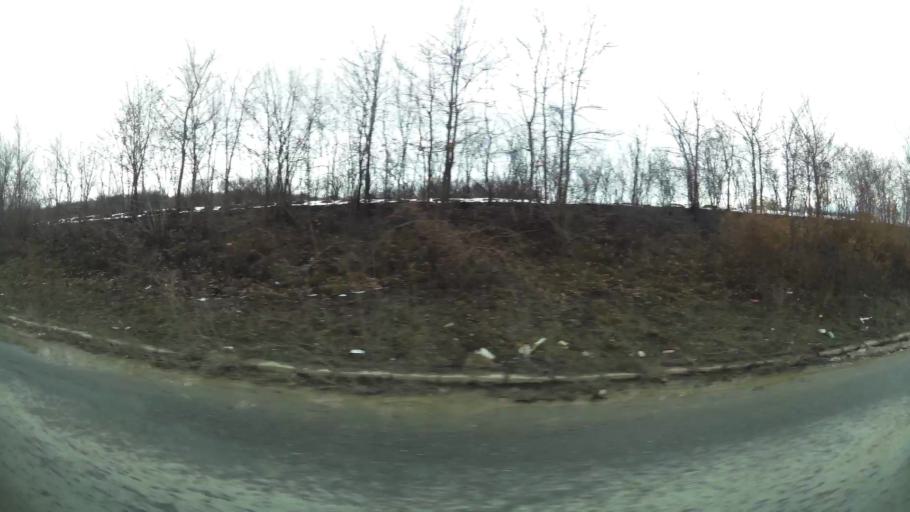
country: RS
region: Central Serbia
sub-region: Belgrade
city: Rakovica
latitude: 44.7218
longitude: 20.4020
